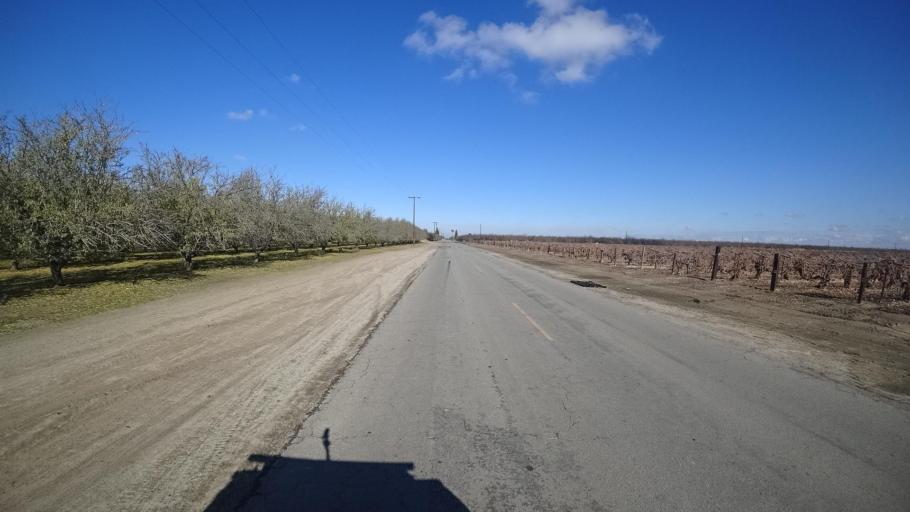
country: US
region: California
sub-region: Kern County
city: McFarland
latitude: 35.6905
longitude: -119.2587
